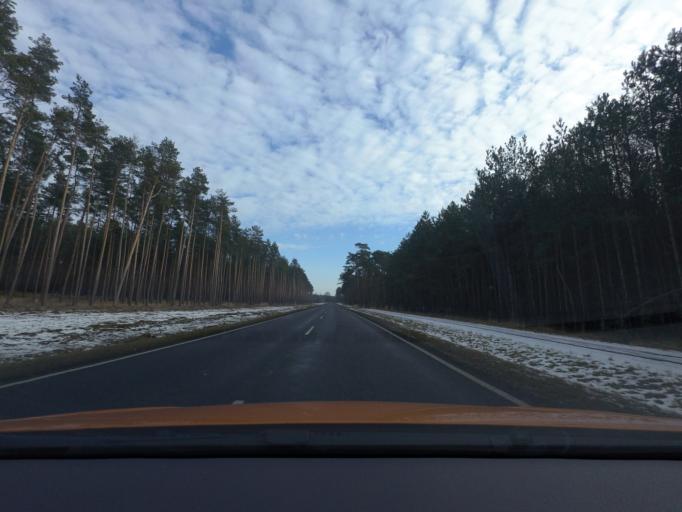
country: DE
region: Brandenburg
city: Ruthnick
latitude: 52.8994
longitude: 13.0746
